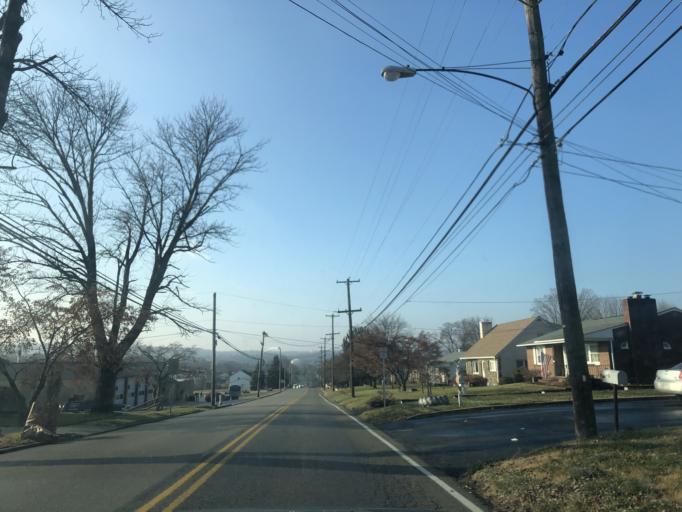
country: US
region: Pennsylvania
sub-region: Montgomery County
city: Conshohocken
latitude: 40.0905
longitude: -75.3020
